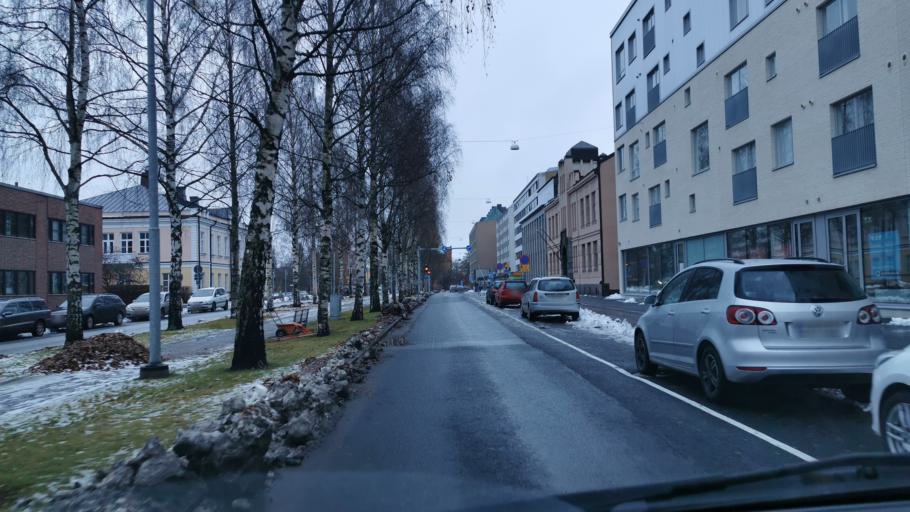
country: FI
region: Ostrobothnia
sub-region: Vaasa
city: Vaasa
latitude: 63.0978
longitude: 21.6072
